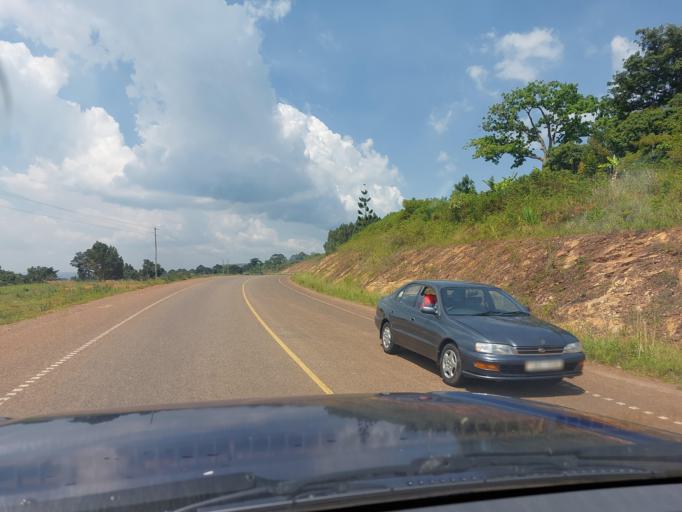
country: UG
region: Central Region
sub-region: Buikwe District
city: Buikwe
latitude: 0.2943
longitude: 33.0929
